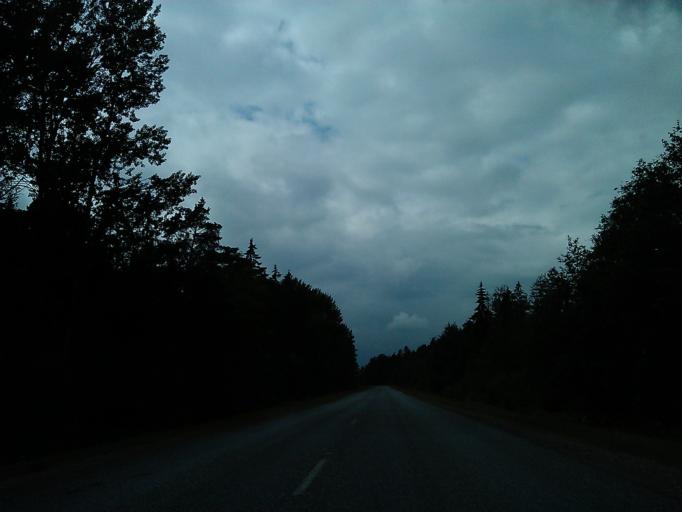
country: LV
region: Kuldigas Rajons
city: Kuldiga
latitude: 56.9830
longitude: 22.0378
